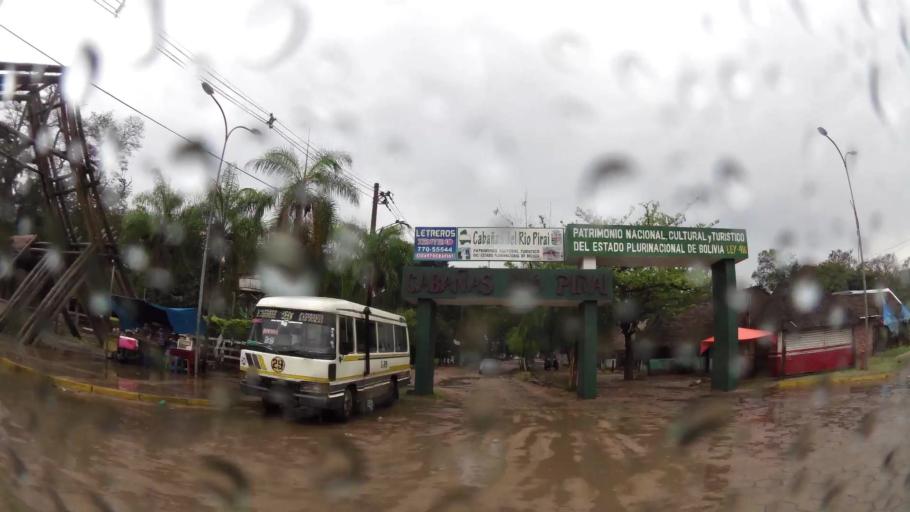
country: BO
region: Santa Cruz
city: Santa Cruz de la Sierra
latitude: -17.7863
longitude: -63.2248
